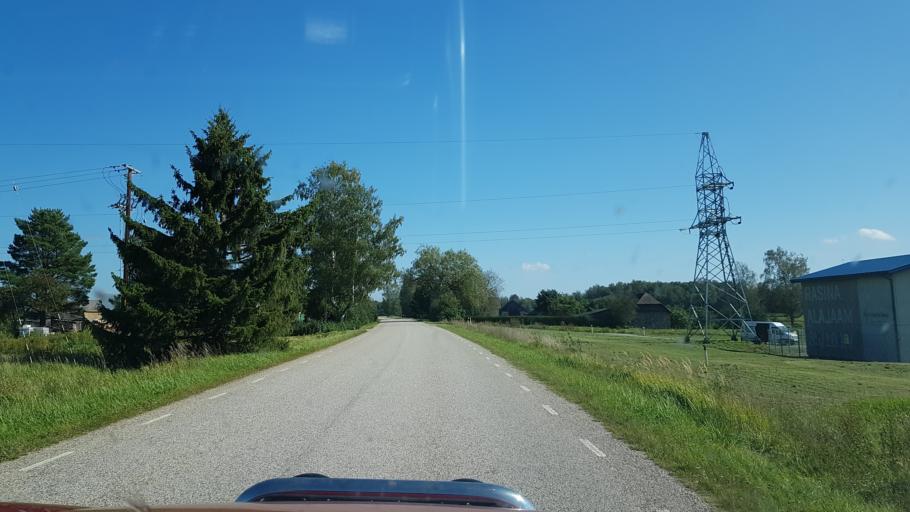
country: EE
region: Polvamaa
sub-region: Raepina vald
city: Rapina
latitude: 58.2109
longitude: 27.2601
